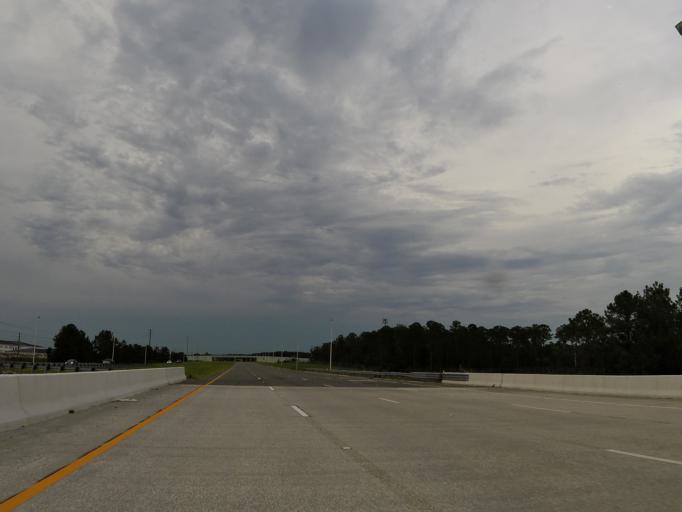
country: US
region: Florida
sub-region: Clay County
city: Lakeside
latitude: 30.1644
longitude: -81.8310
